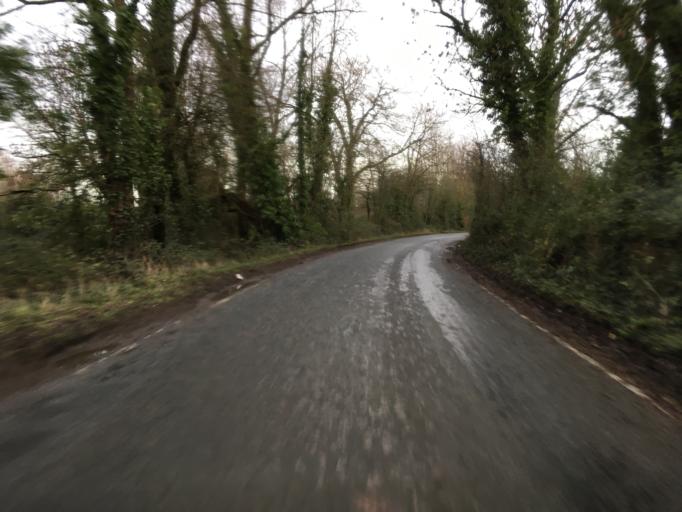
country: GB
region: Wales
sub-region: Newport
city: Goldcliff
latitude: 51.5429
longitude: -2.9038
